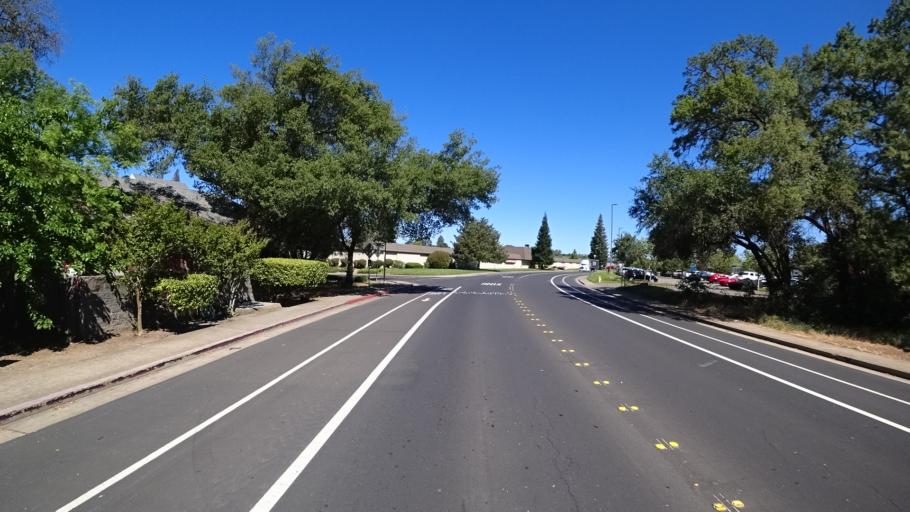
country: US
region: California
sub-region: Placer County
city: Rocklin
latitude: 38.7958
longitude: -121.2232
